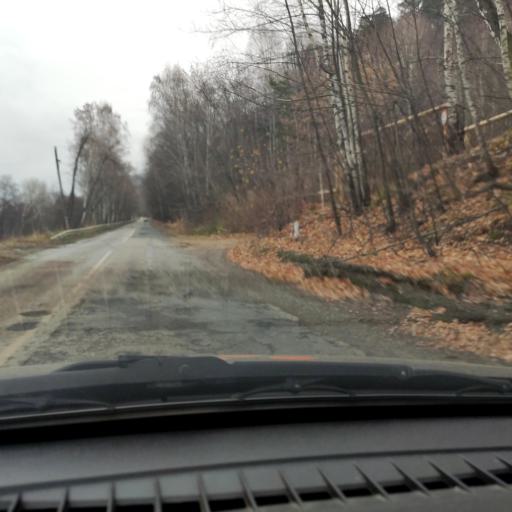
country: RU
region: Samara
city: Pribrezhnyy
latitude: 53.4382
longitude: 49.7109
